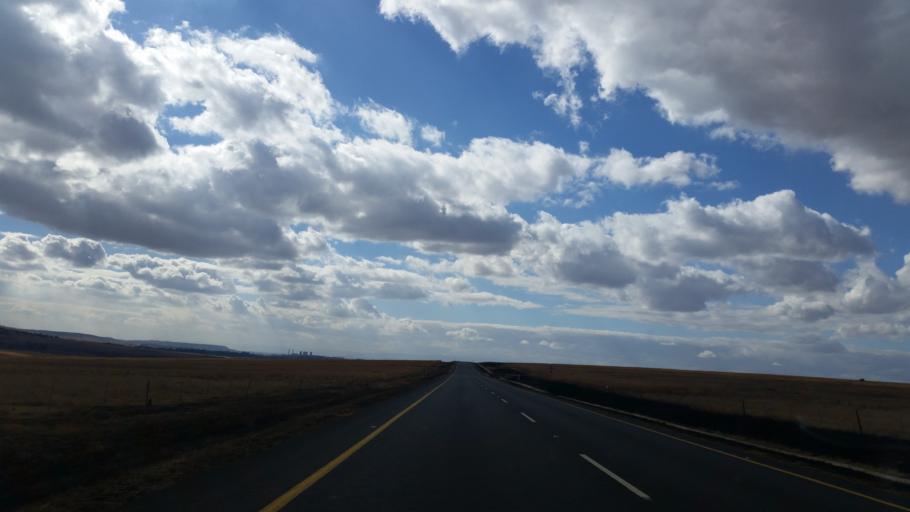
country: ZA
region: KwaZulu-Natal
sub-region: Amajuba District Municipality
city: Dannhauser
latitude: -27.9521
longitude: 29.9716
